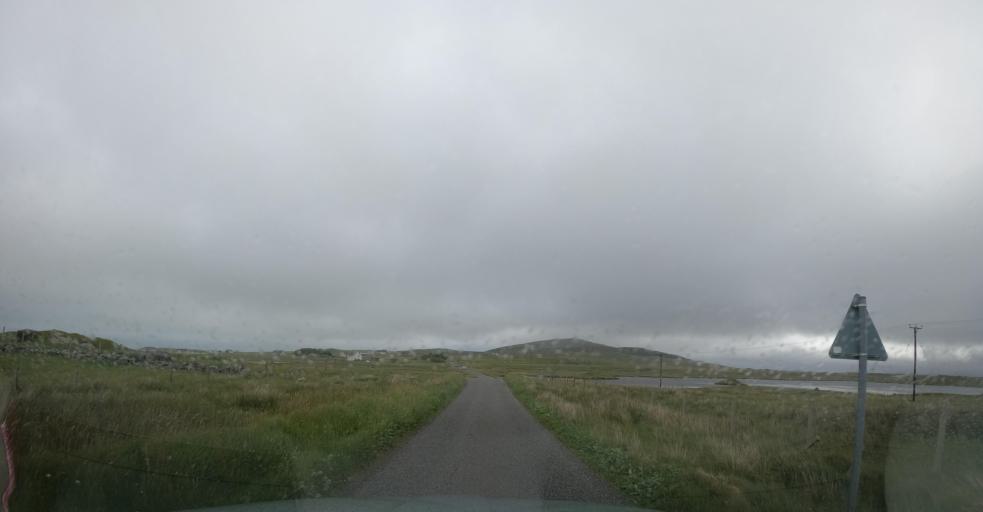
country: GB
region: Scotland
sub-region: Eilean Siar
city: Isle of North Uist
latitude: 57.6528
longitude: -7.2474
